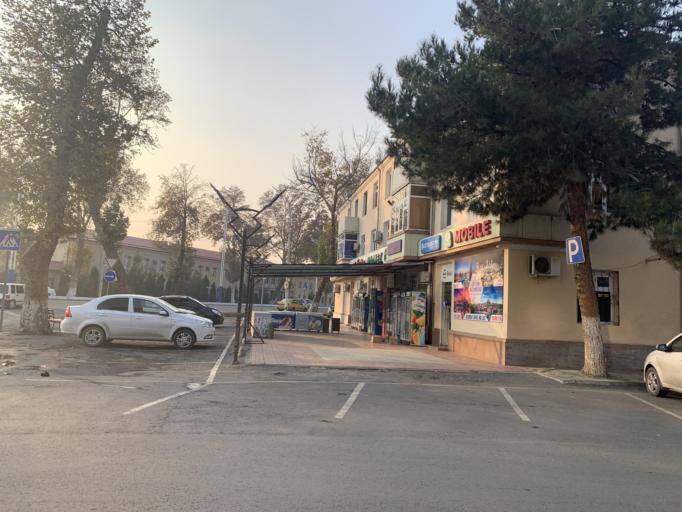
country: UZ
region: Fergana
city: Qo`qon
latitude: 40.5198
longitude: 70.9380
